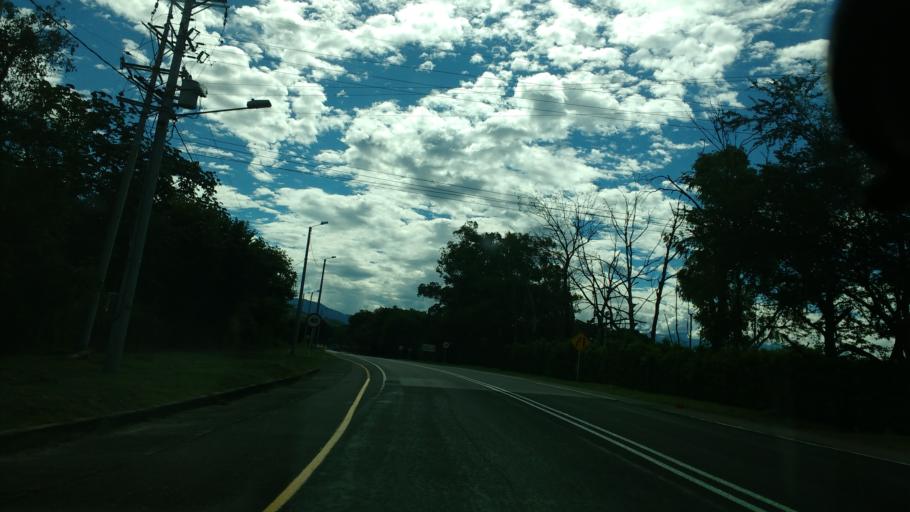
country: CO
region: Tolima
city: Valle de San Juan
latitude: 4.3273
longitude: -75.0750
